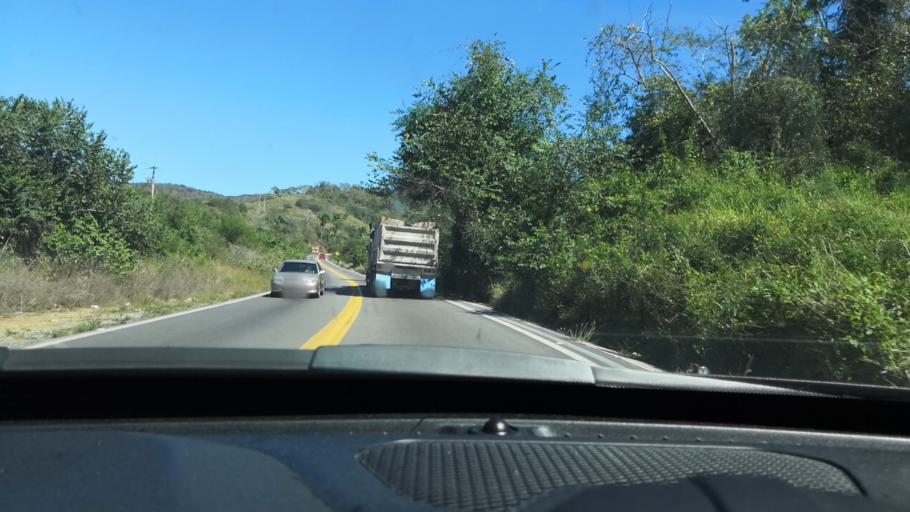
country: MX
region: Nayarit
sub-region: Bahia de Banderas
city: Lo de Marcos
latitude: 20.9072
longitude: -105.3869
